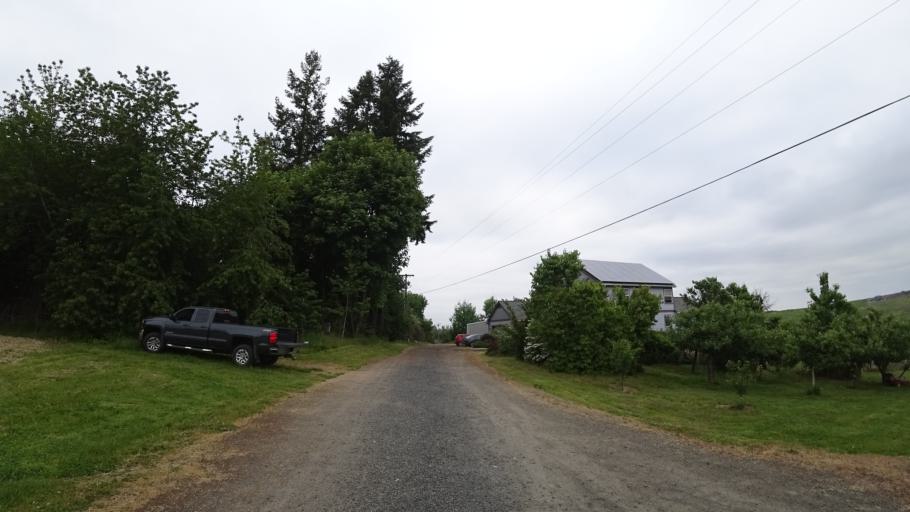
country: US
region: Oregon
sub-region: Washington County
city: Hillsboro
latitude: 45.4951
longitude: -122.9864
